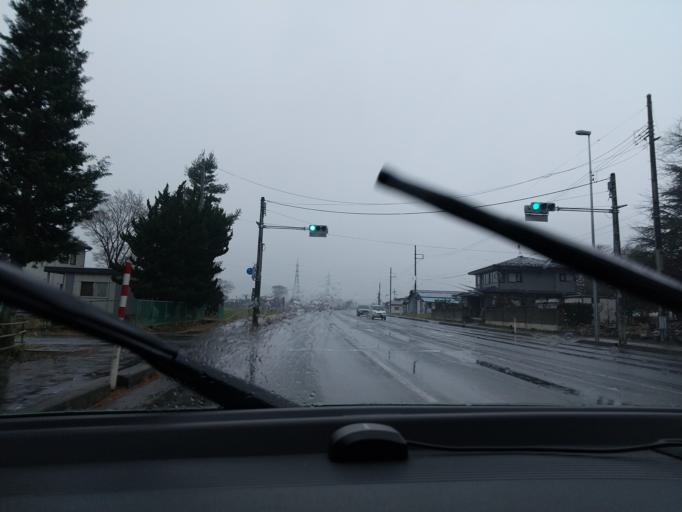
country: JP
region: Iwate
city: Morioka-shi
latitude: 39.6927
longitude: 141.0972
